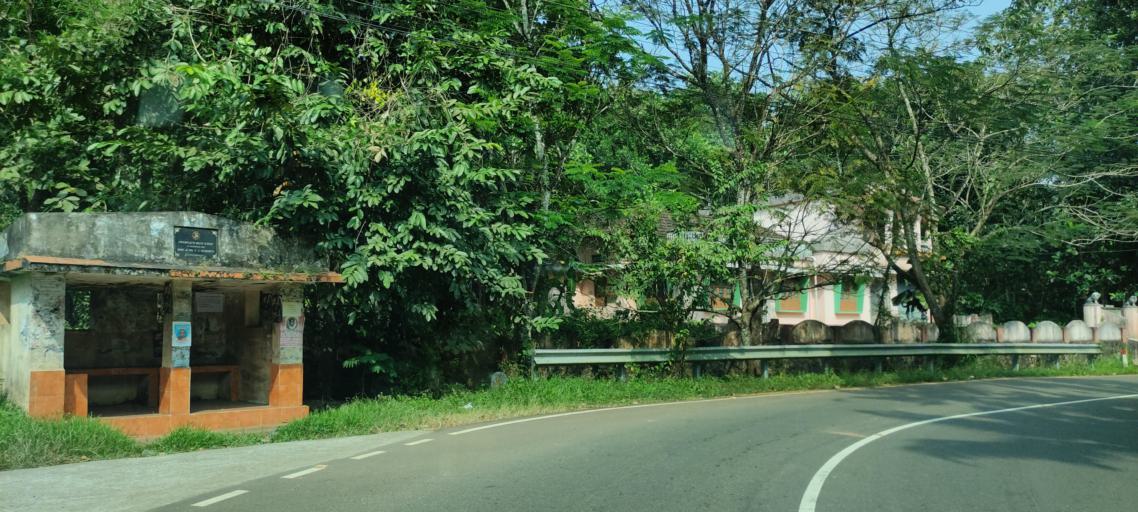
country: IN
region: Kerala
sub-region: Pattanamtitta
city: Adur
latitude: 9.2281
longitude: 76.7049
